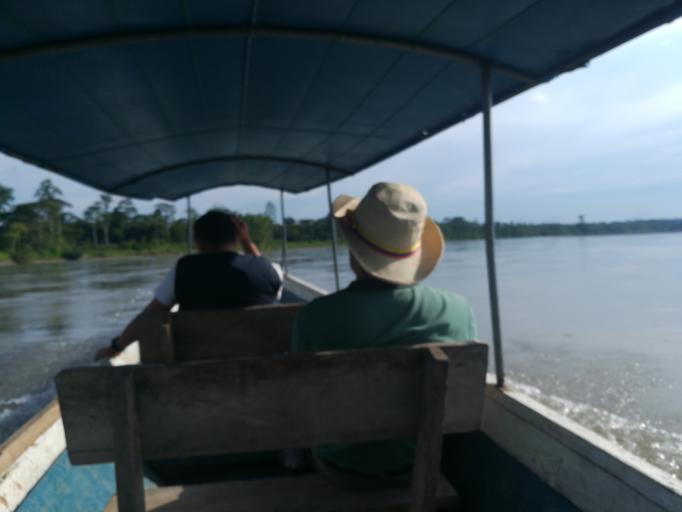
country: EC
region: Orellana
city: Boca Suno
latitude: -0.8365
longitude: -77.1941
